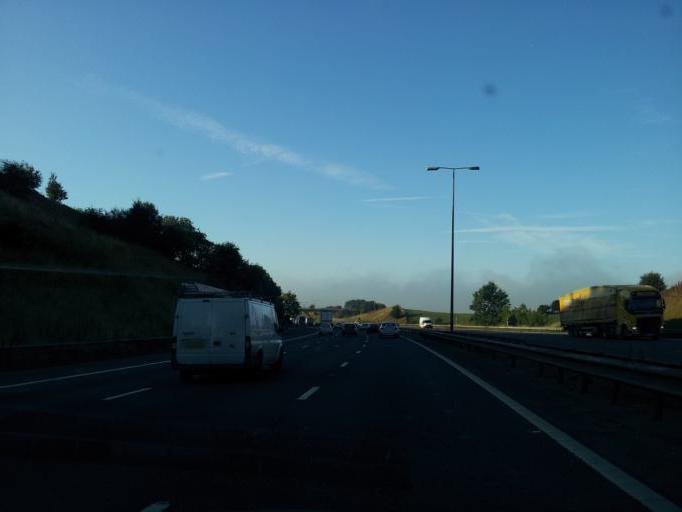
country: GB
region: England
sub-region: Borough of Rochdale
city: Littleborough
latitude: 53.6191
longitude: -2.0853
